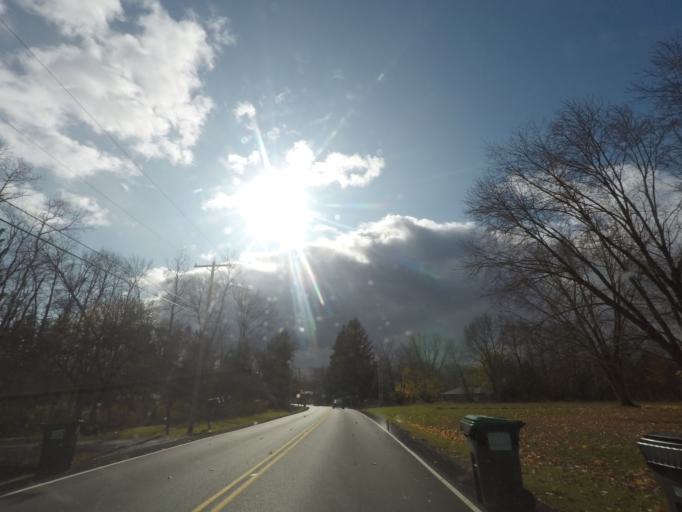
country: US
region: New York
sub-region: Saratoga County
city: Country Knolls
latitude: 42.9302
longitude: -73.8553
